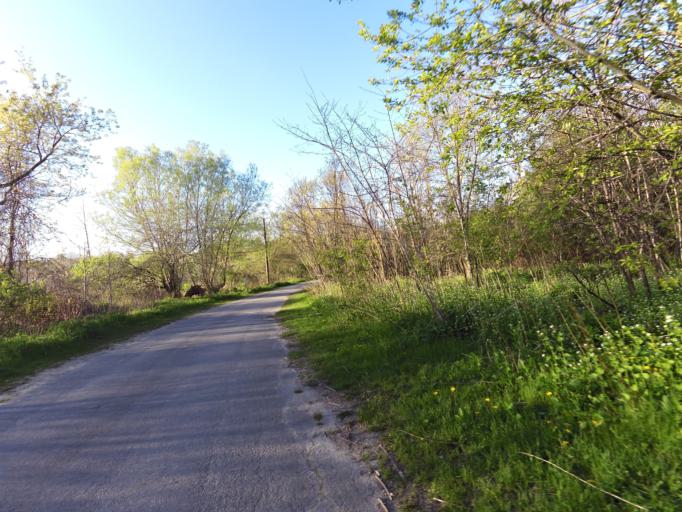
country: CA
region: Ontario
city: Toronto
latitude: 43.6923
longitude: -79.3598
